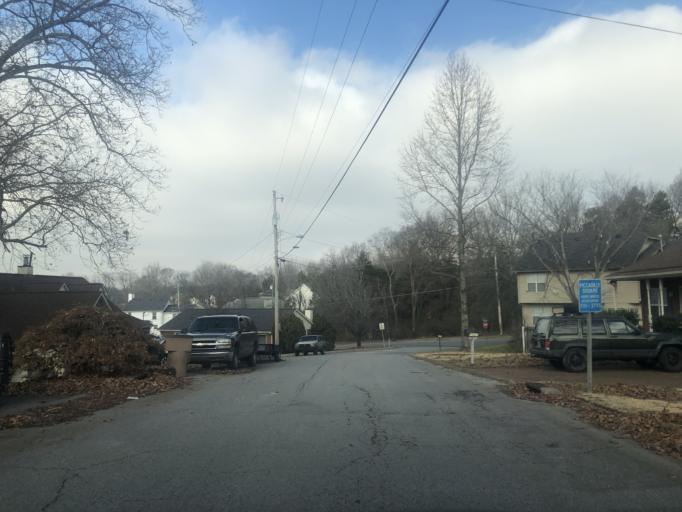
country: US
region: Tennessee
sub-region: Rutherford County
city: La Vergne
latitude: 36.0834
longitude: -86.6581
